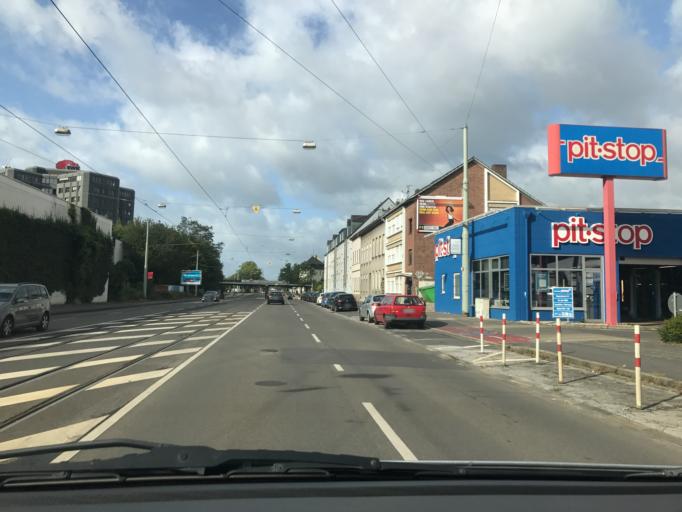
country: DE
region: North Rhine-Westphalia
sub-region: Regierungsbezirk Dusseldorf
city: Krefeld
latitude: 51.3302
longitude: 6.5432
